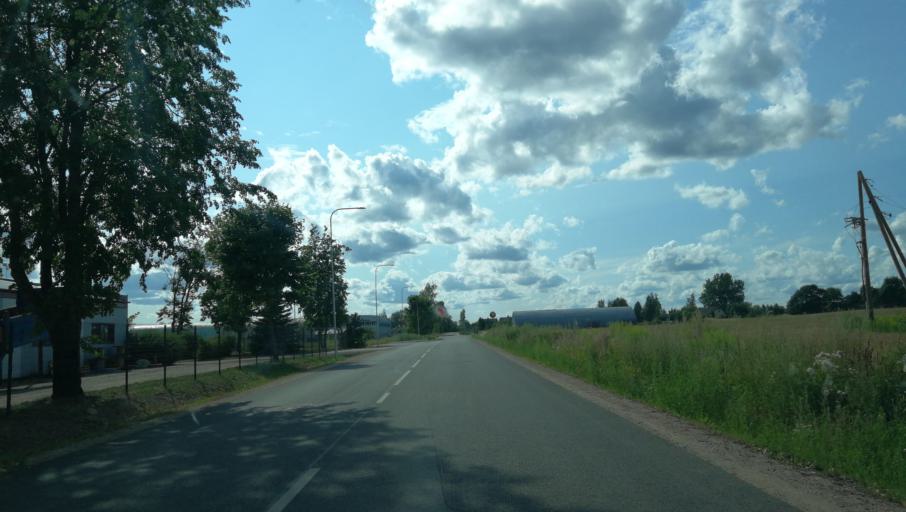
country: LV
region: Cesu Rajons
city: Cesis
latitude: 57.3229
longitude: 25.3066
